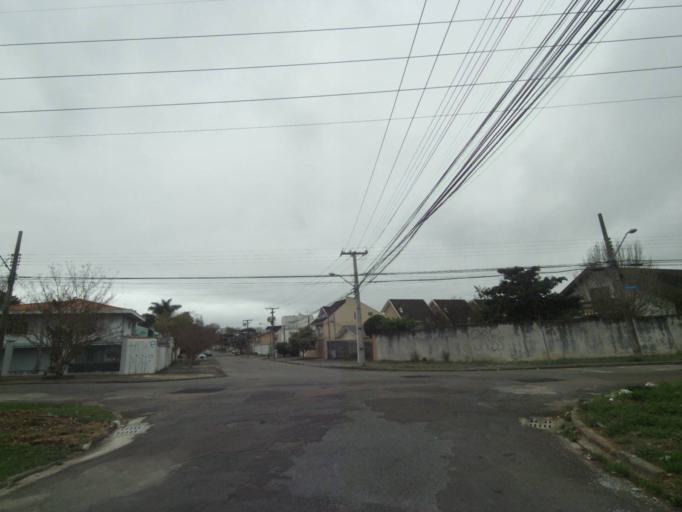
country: BR
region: Parana
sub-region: Curitiba
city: Curitiba
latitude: -25.4713
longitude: -49.2820
